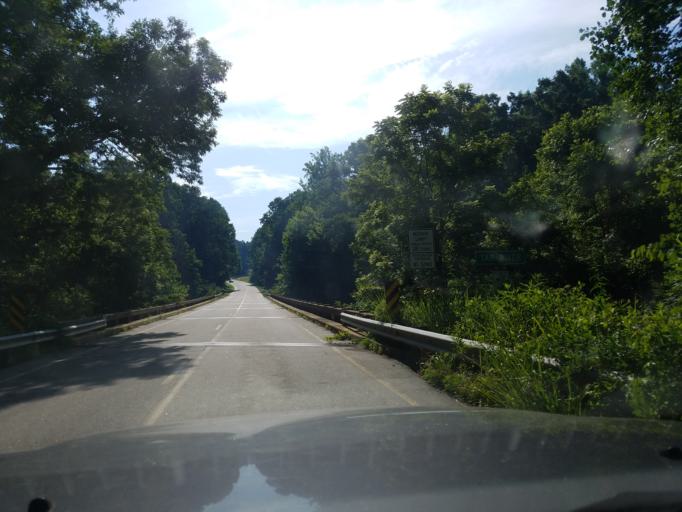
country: US
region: North Carolina
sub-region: Granville County
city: Oxford
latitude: 36.2504
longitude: -78.6721
